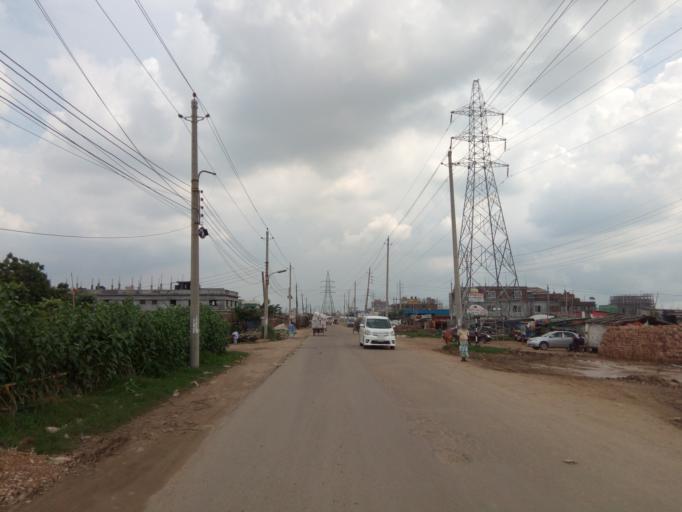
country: BD
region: Dhaka
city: Azimpur
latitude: 23.7358
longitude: 90.3618
